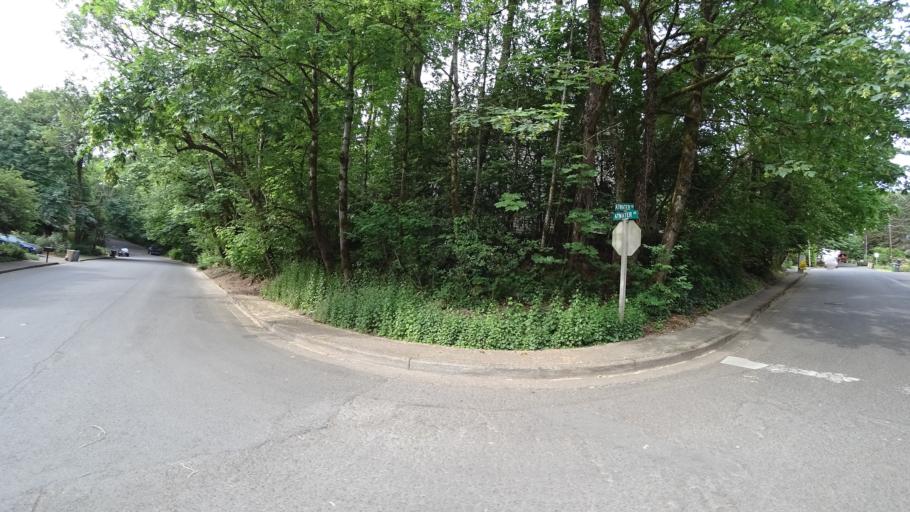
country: US
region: Oregon
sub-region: Clackamas County
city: Lake Oswego
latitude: 45.4257
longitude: -122.6814
